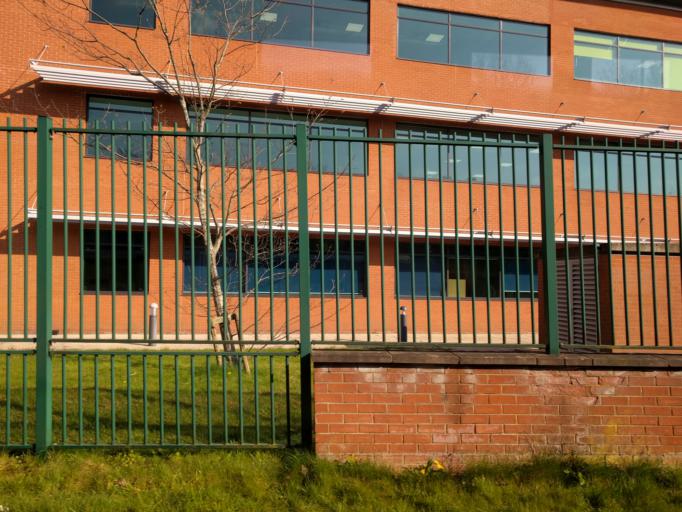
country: GB
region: England
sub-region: Manchester
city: Ringway
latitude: 53.3725
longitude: -2.2491
